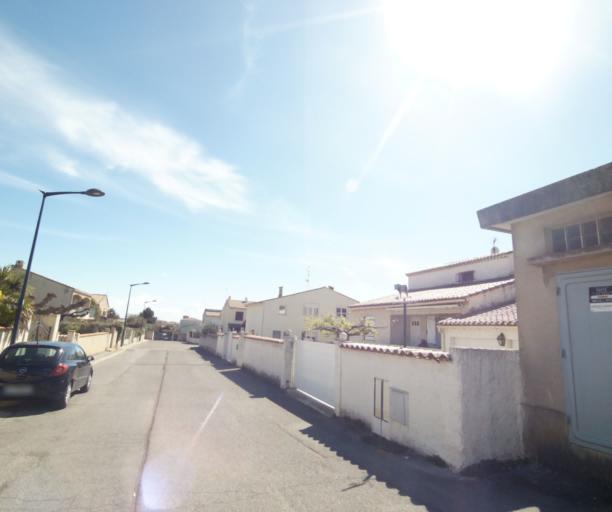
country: FR
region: Languedoc-Roussillon
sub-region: Departement de l'Herault
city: Villeneuve-les-Maguelone
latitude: 43.5317
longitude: 3.8562
